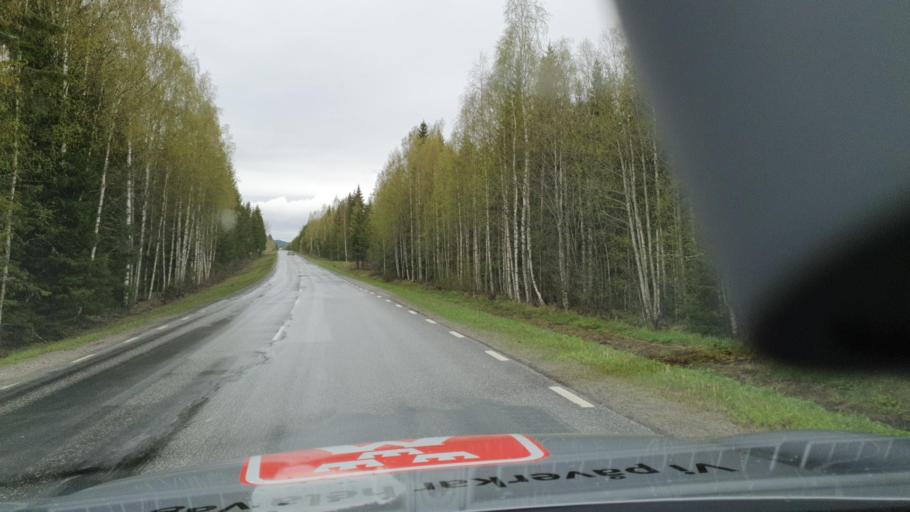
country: SE
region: Vaesternorrland
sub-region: OErnskoeldsviks Kommun
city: Bjasta
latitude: 63.4038
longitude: 18.4537
